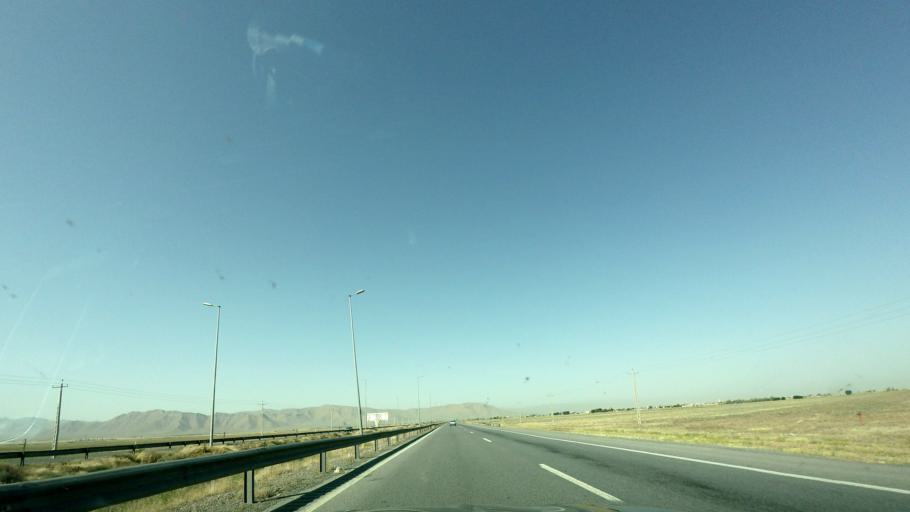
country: IR
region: Markazi
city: Ashtian
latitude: 34.1781
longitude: 50.0425
